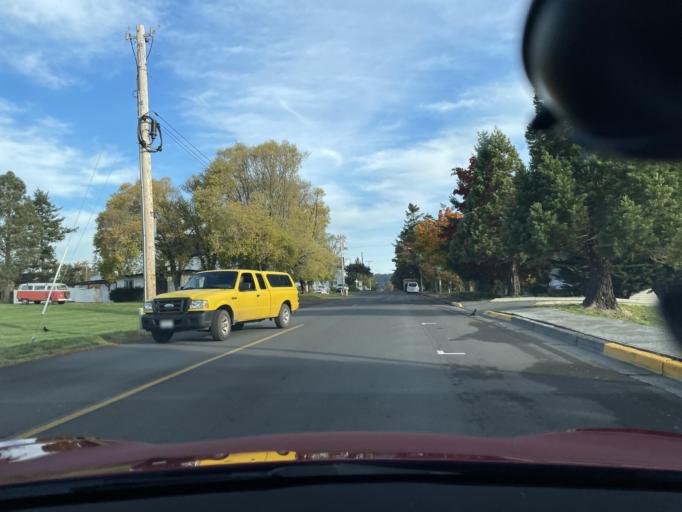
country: US
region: Washington
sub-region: San Juan County
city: Friday Harbor
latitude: 48.5315
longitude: -123.0244
